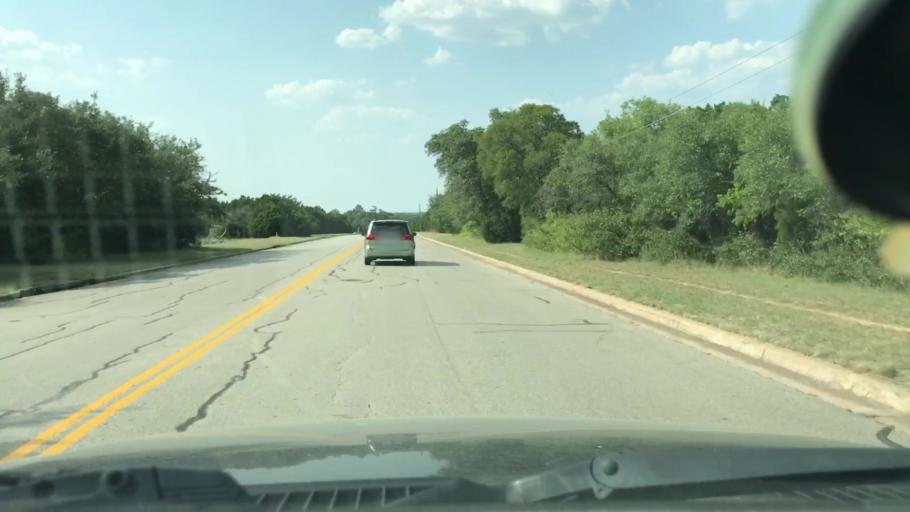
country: US
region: Texas
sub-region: Williamson County
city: Cedar Park
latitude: 30.5361
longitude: -97.8308
